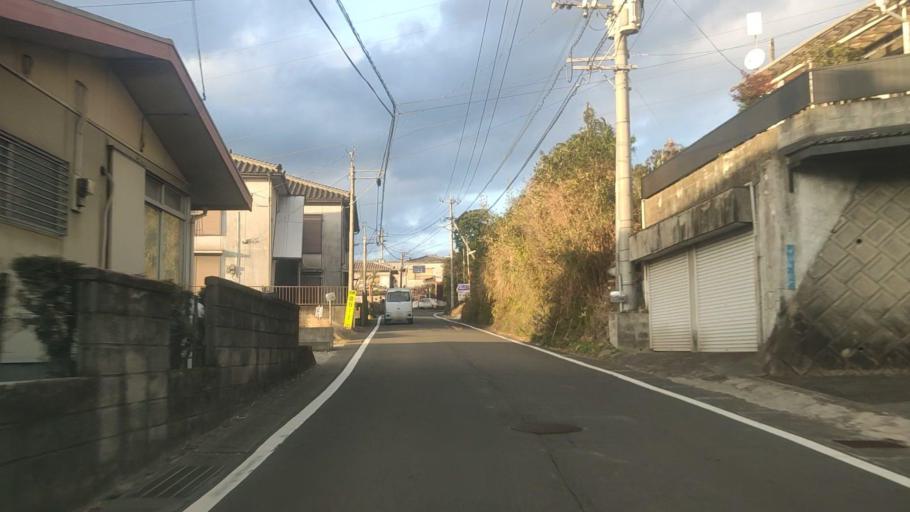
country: JP
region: Kagoshima
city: Kagoshima-shi
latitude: 31.6231
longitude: 130.5528
